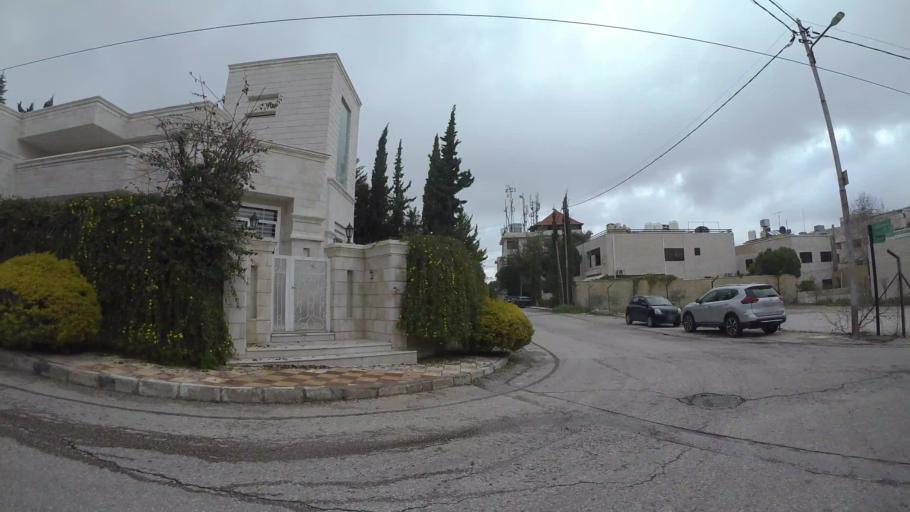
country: JO
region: Amman
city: Amman
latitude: 31.9467
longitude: 35.8998
